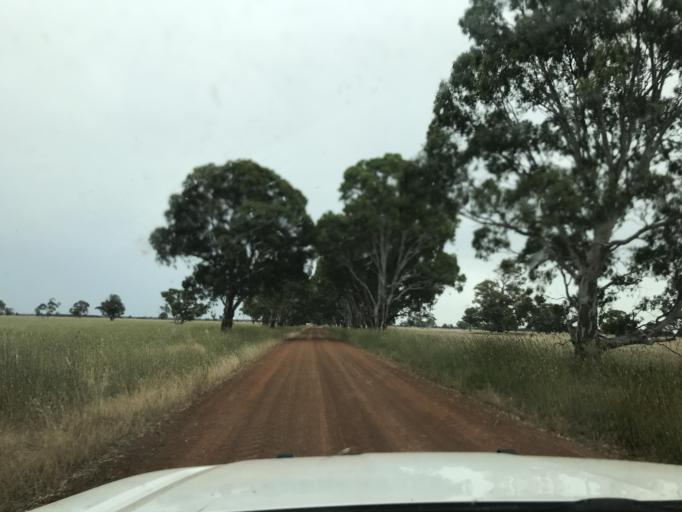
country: AU
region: Victoria
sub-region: Horsham
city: Horsham
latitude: -37.0625
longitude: 141.6304
